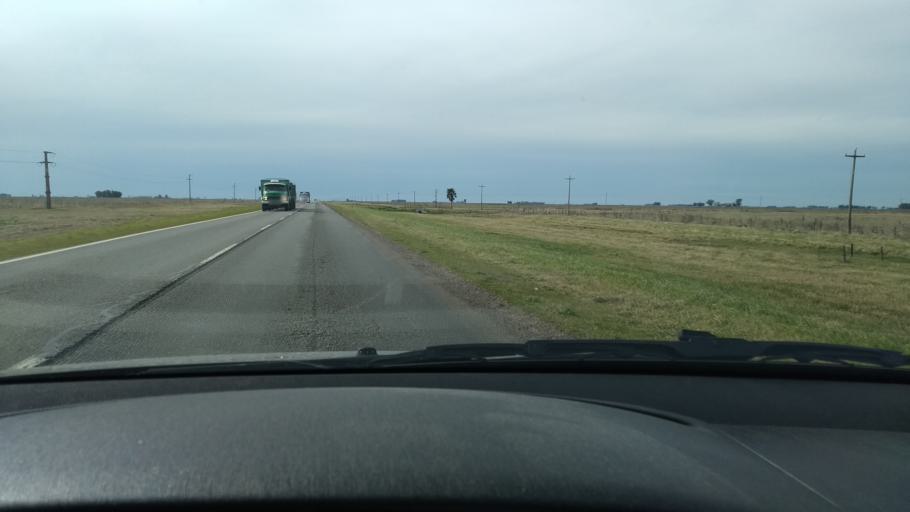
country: AR
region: Buenos Aires
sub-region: Partido de Azul
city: Azul
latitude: -36.6947
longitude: -59.7432
